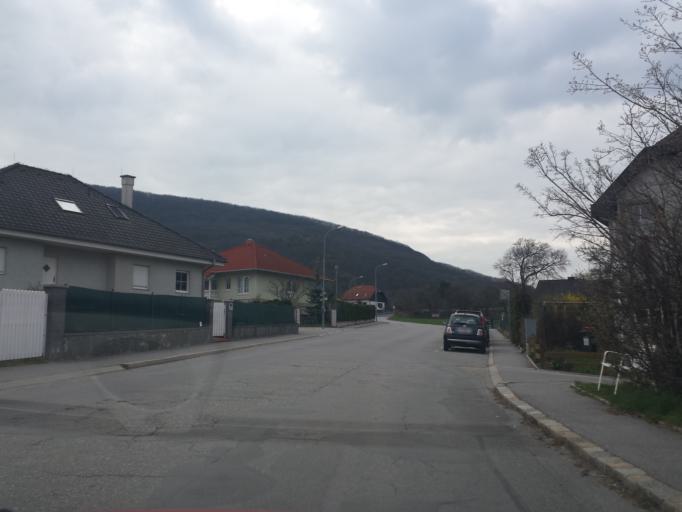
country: AT
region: Lower Austria
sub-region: Politischer Bezirk Bruck an der Leitha
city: Hainburg an der Donau
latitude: 48.1405
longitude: 16.9516
